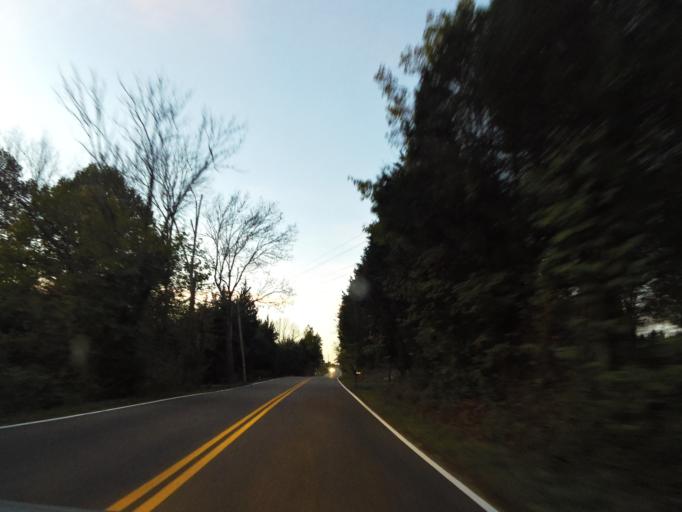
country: US
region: Tennessee
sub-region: Knox County
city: Mascot
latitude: 35.9919
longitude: -83.6331
